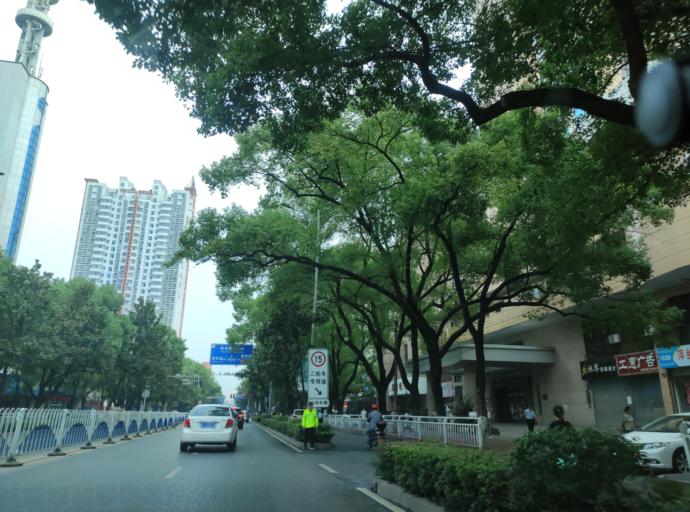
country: CN
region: Jiangxi Sheng
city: Pingxiang
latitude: 27.6430
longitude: 113.8404
